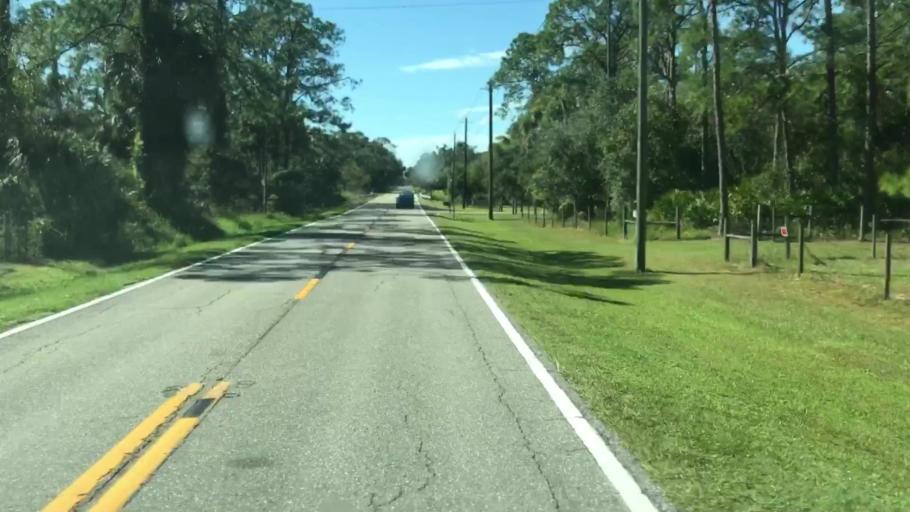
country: US
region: Florida
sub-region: Lee County
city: Olga
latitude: 26.7248
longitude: -81.6670
